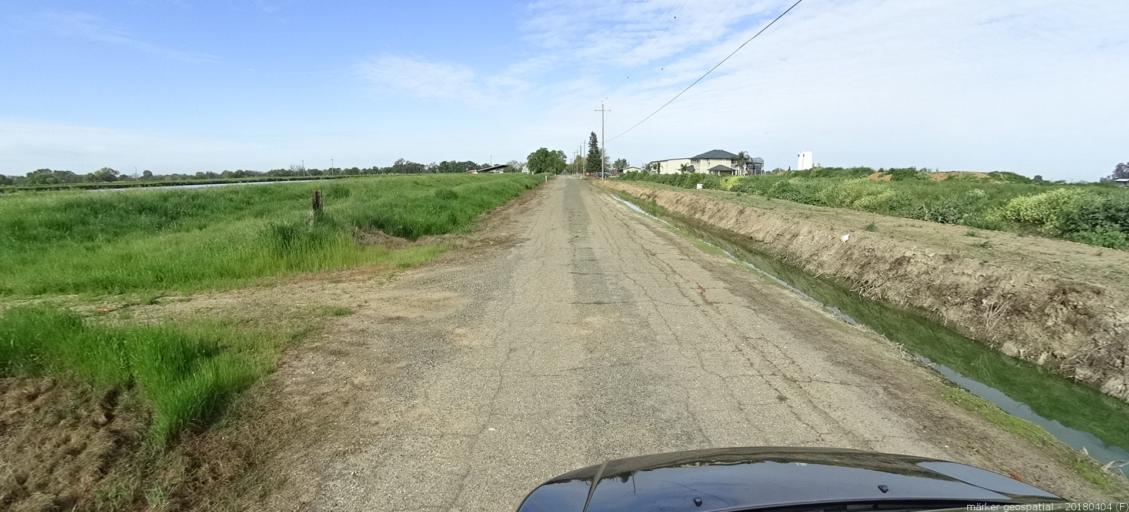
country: US
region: California
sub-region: Sacramento County
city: Herald
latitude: 38.2559
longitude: -121.2182
